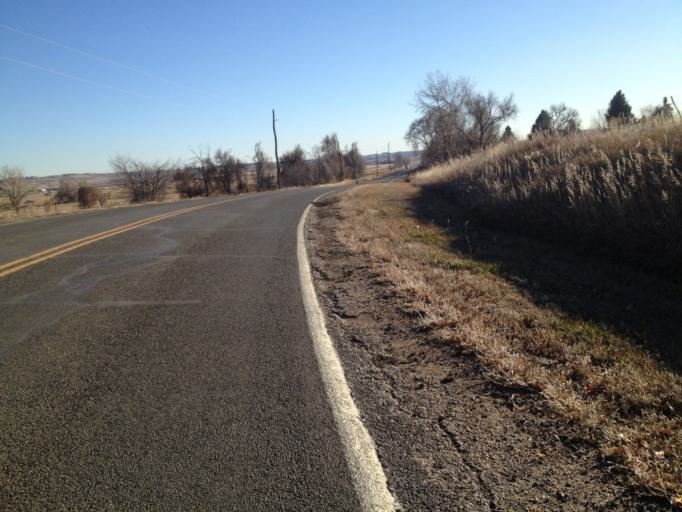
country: US
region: Colorado
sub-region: Boulder County
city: Louisville
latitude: 39.9754
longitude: -105.1093
